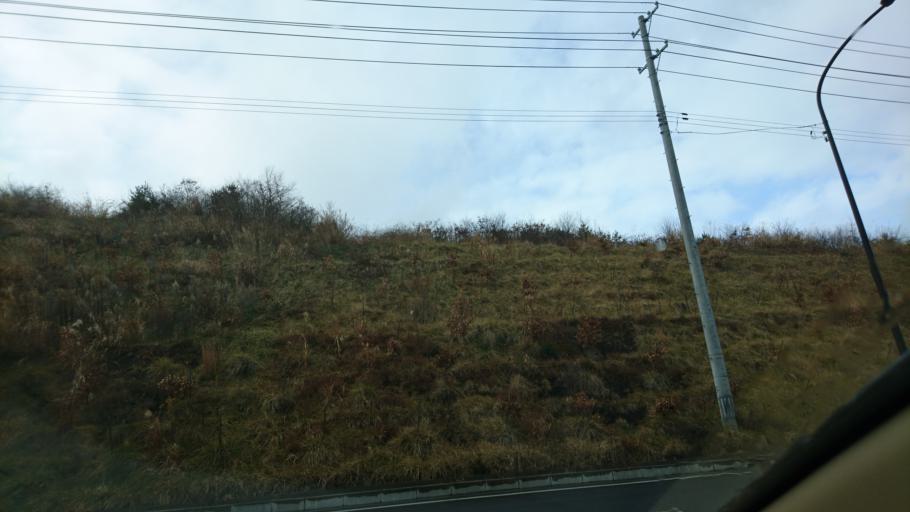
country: JP
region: Miyagi
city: Tomiya
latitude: 38.3928
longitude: 140.8754
